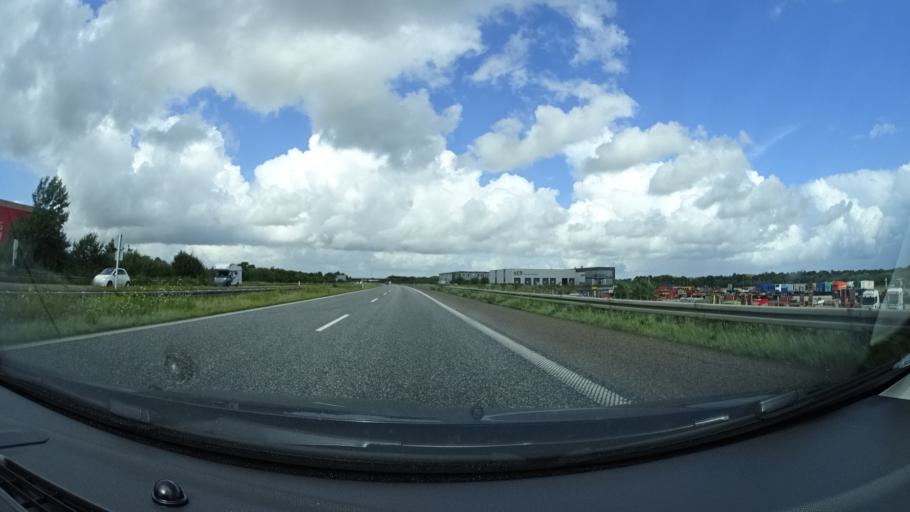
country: DK
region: South Denmark
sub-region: Aabenraa Kommune
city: Rodekro
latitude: 55.0756
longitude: 9.3702
